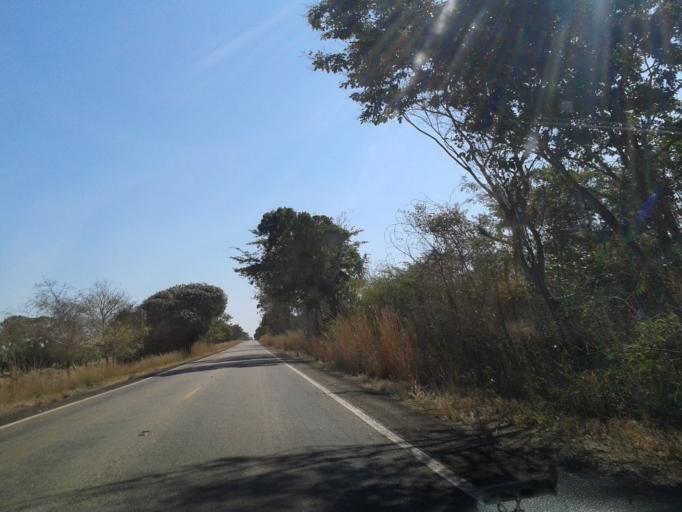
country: BR
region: Goias
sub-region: Mozarlandia
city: Mozarlandia
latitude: -14.2899
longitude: -50.4023
